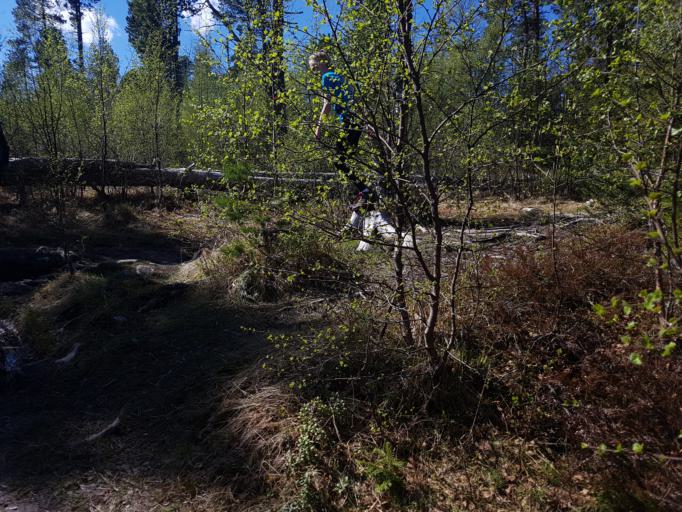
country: NO
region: Sor-Trondelag
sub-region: Trondheim
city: Trondheim
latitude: 63.4264
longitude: 10.3156
